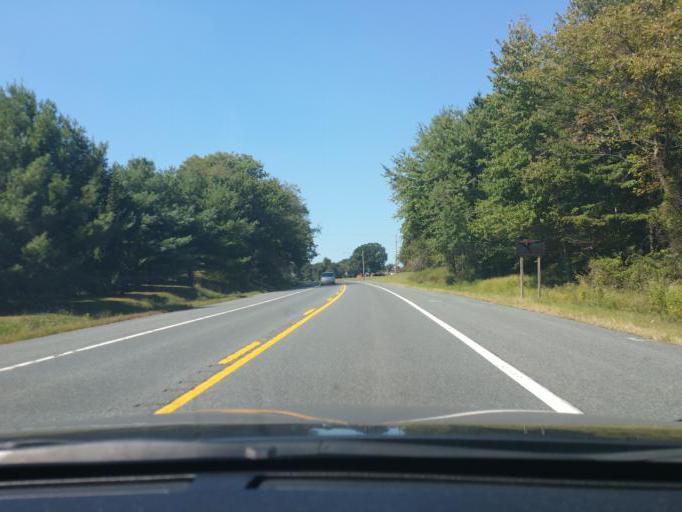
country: US
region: Maryland
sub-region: Harford County
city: Havre de Grace
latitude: 39.5745
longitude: -76.1463
